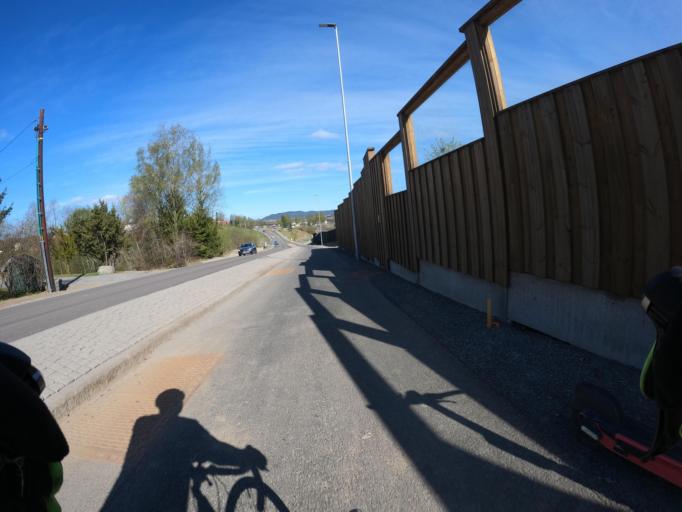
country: NO
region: Akershus
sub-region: Lorenskog
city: Kjenn
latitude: 59.9662
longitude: 10.9944
